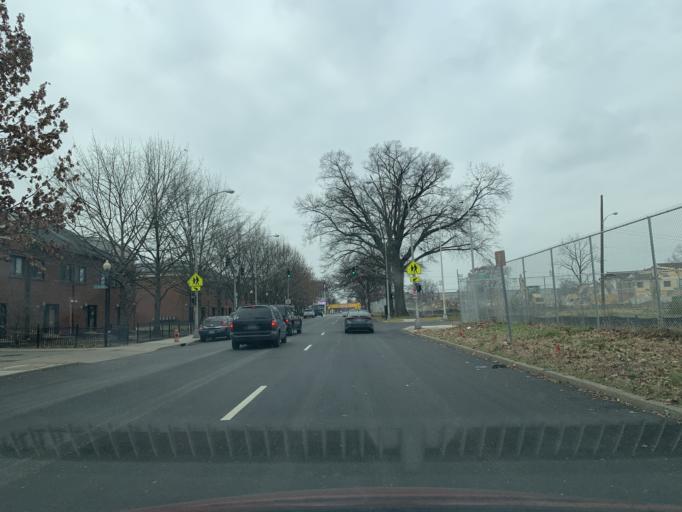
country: US
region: Kentucky
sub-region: Jefferson County
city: Louisville
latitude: 38.2526
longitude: -85.7702
